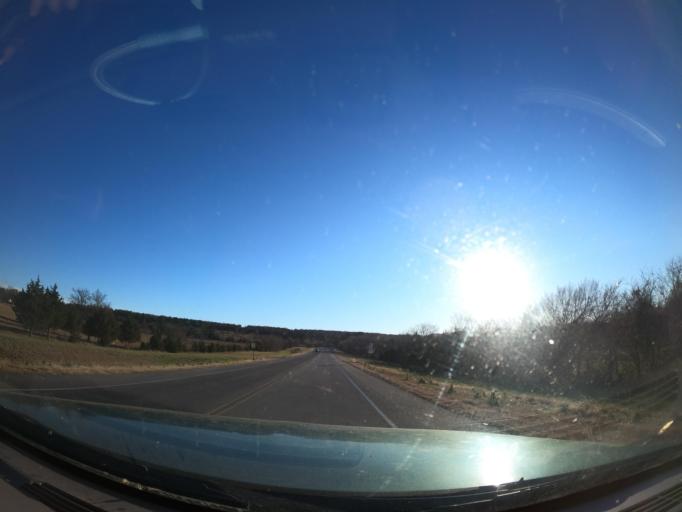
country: US
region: Oklahoma
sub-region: Pittsburg County
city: Hartshorne
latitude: 34.8444
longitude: -95.5386
